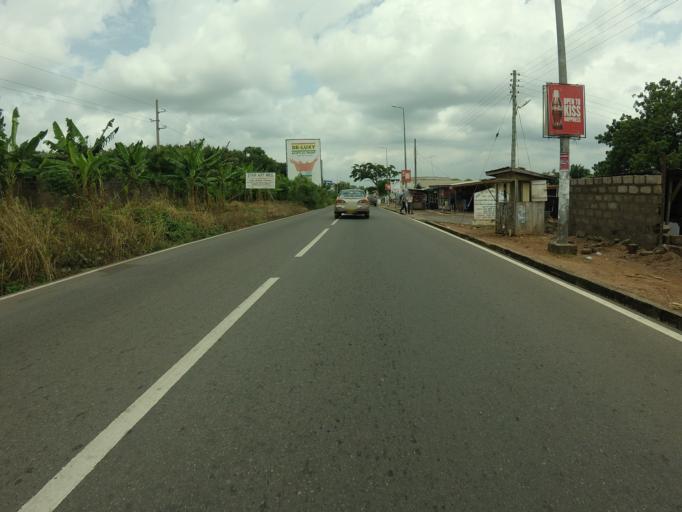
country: GH
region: Volta
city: Ho
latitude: 6.5959
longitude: 0.4723
